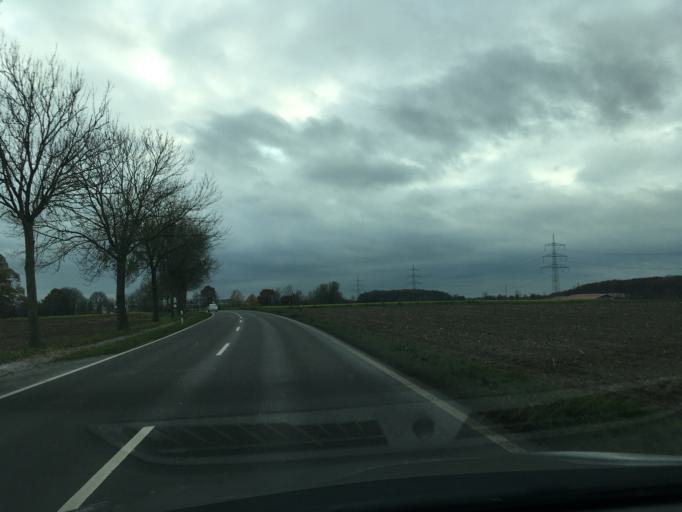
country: DE
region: North Rhine-Westphalia
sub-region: Regierungsbezirk Munster
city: Ahaus
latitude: 52.0922
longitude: 6.9654
